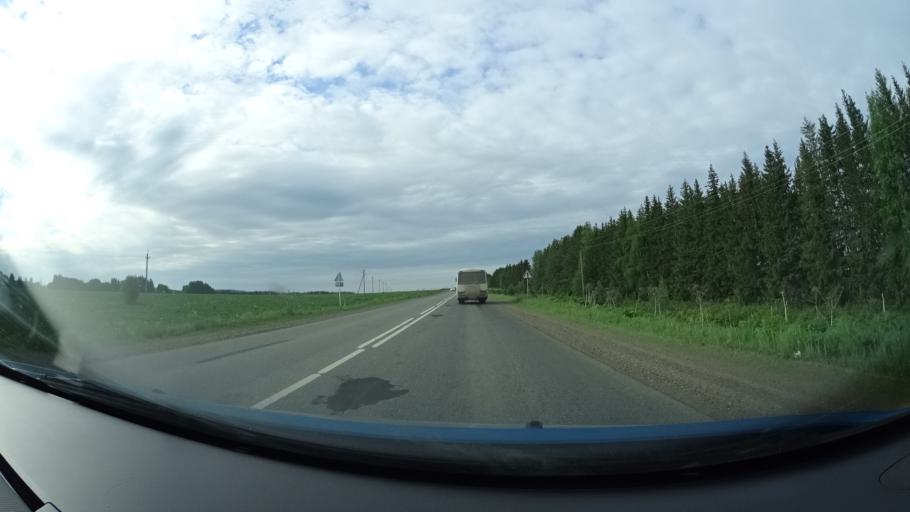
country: RU
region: Perm
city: Osa
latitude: 57.2718
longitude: 55.5704
